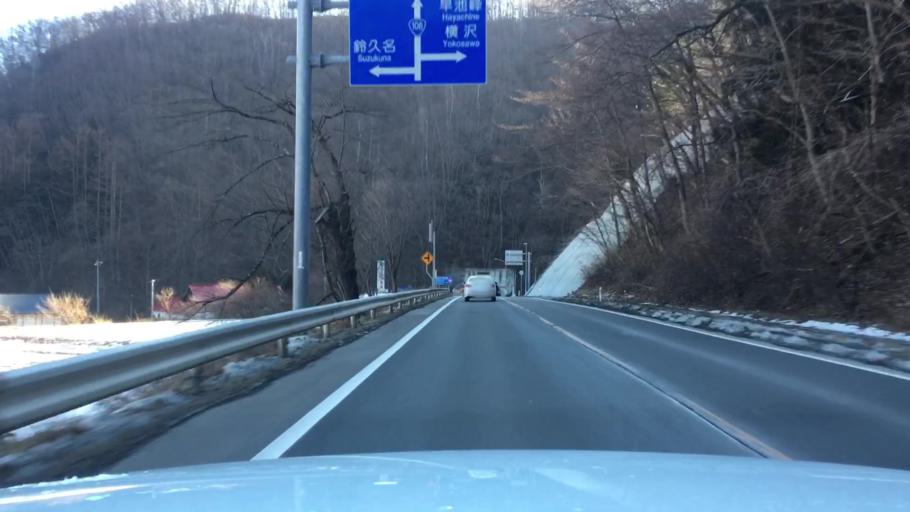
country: JP
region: Iwate
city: Tono
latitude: 39.6228
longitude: 141.6135
